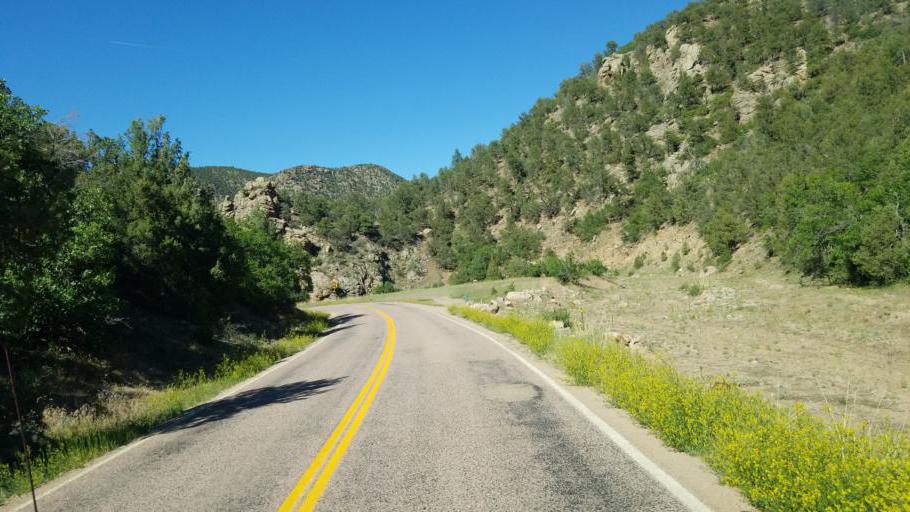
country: US
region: Colorado
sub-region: Fremont County
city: Canon City
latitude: 38.4057
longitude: -105.4390
